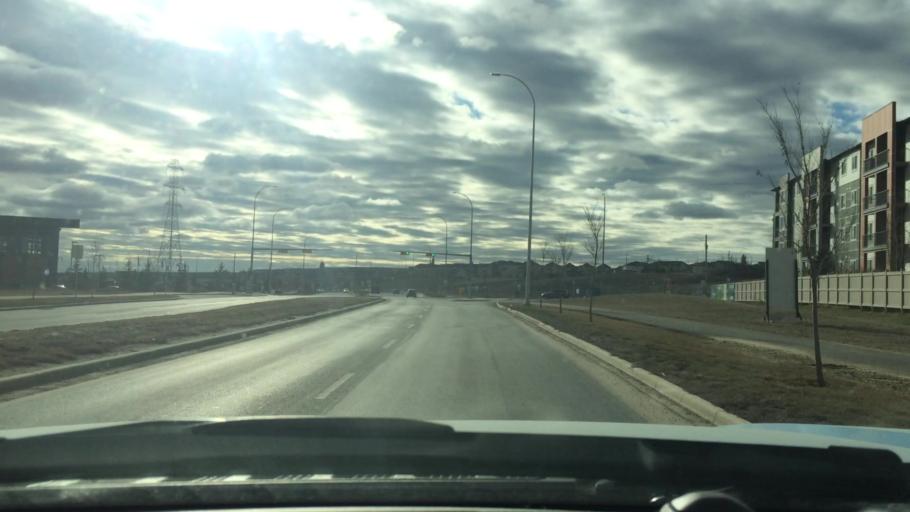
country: CA
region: Alberta
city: Calgary
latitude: 51.1709
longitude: -114.1336
